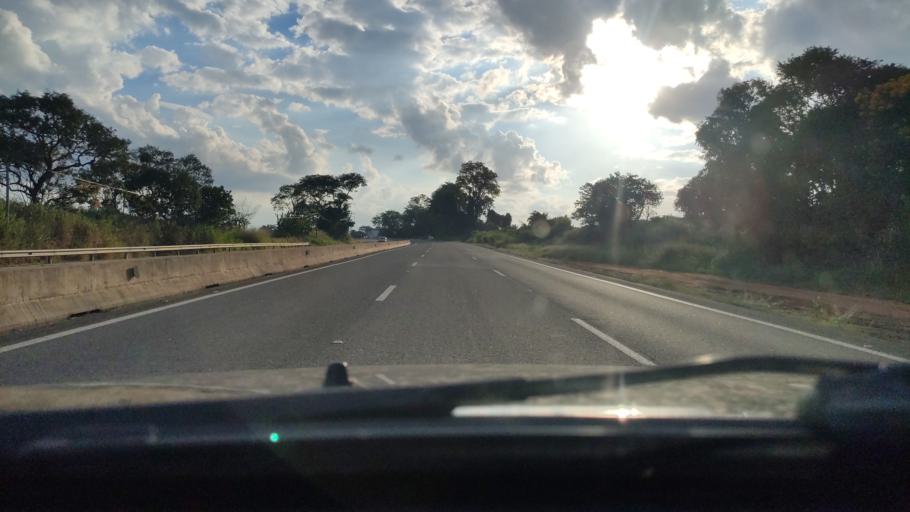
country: BR
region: Sao Paulo
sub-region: Mogi-Mirim
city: Mogi Mirim
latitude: -22.4506
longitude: -47.0805
